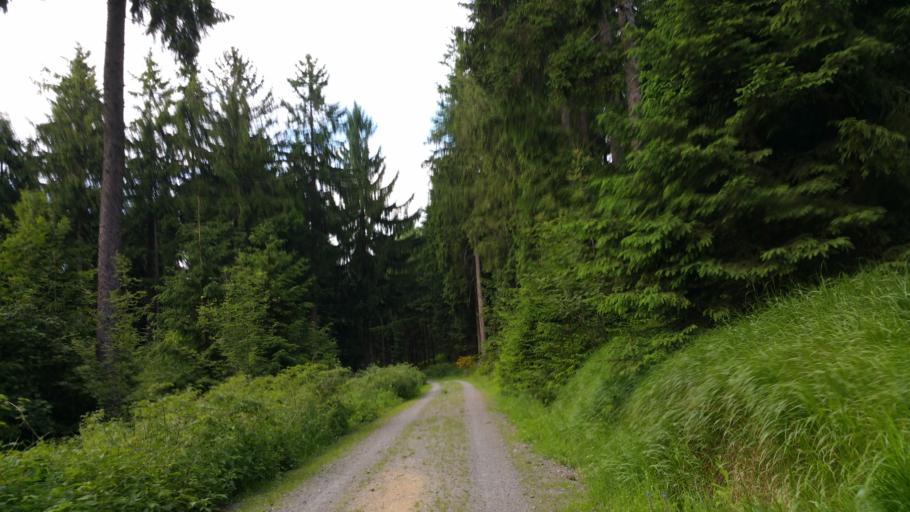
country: DE
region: Bavaria
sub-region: Upper Franconia
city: Marktleuthen
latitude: 50.1847
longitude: 12.0124
